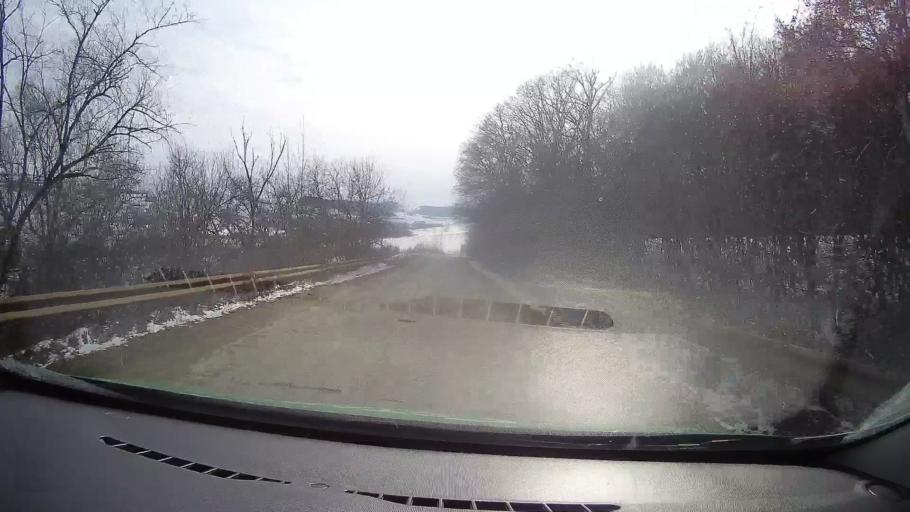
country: RO
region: Sibiu
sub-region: Comuna Bradeni
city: Bradeni
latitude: 46.0980
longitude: 24.8364
